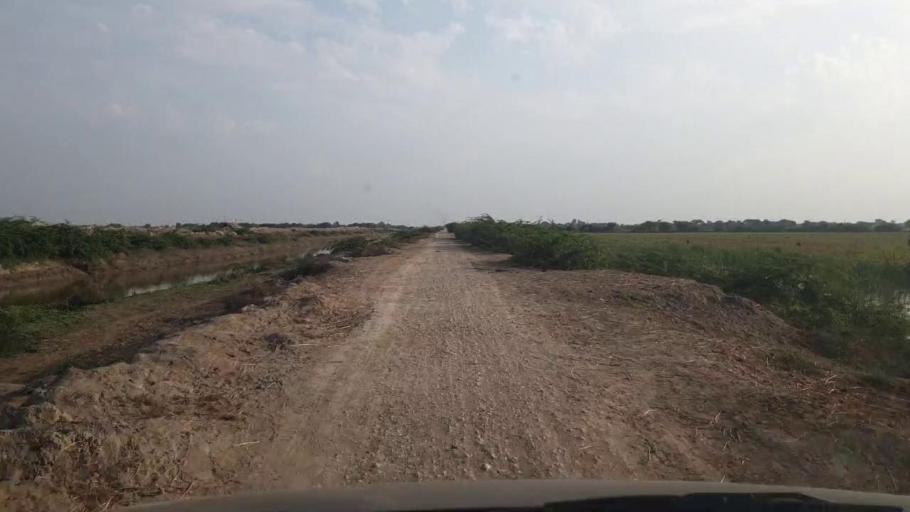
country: PK
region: Sindh
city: Badin
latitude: 24.5548
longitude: 68.6699
